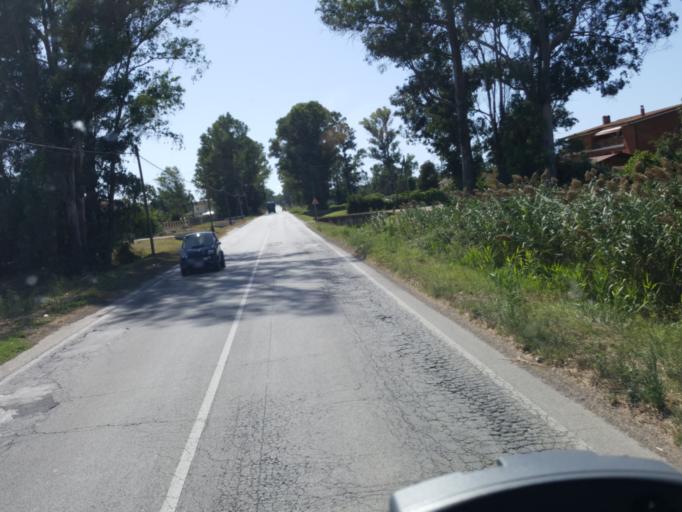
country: IT
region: Latium
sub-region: Provincia di Latina
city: Sabaudia
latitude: 41.3466
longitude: 13.0917
